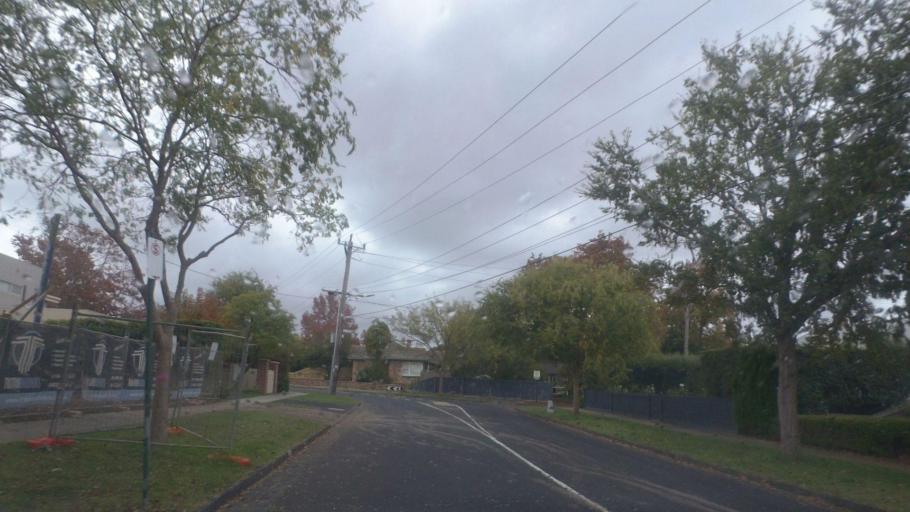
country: AU
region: Victoria
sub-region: Whitehorse
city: Box Hill
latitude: -37.8239
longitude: 145.1318
